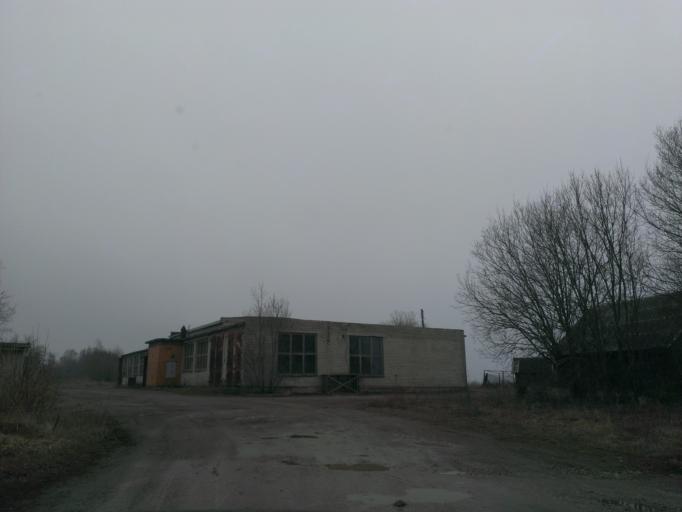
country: EE
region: Laeaene
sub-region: Lihula vald
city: Lihula
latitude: 58.5881
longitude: 23.5249
